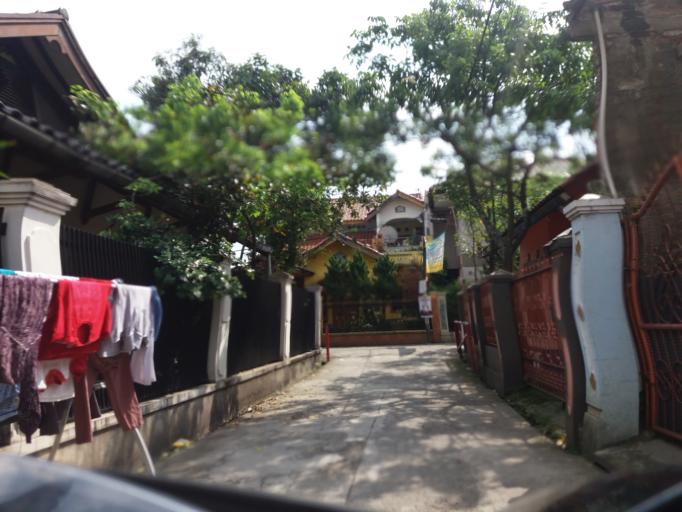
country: ID
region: West Java
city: Bandung
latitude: -6.9247
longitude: 107.6577
